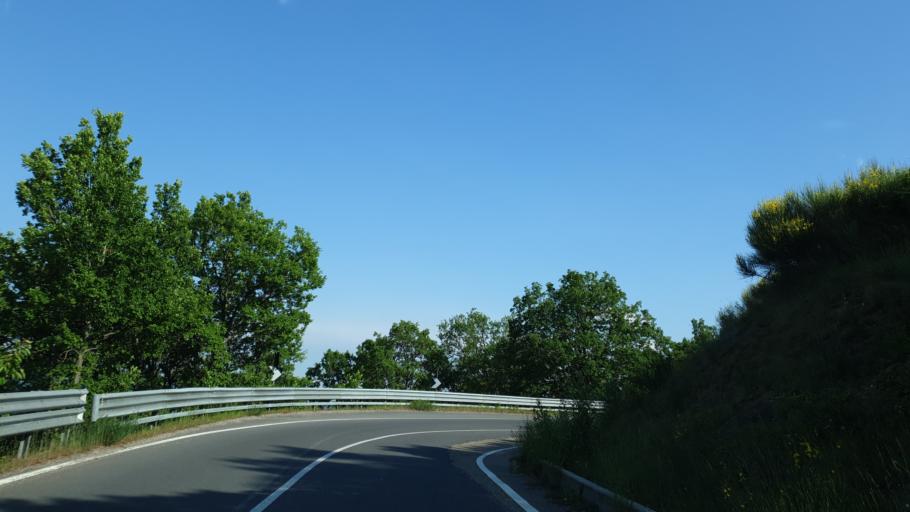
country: IT
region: Tuscany
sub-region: Province of Arezzo
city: Stia
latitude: 43.7754
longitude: 11.6914
